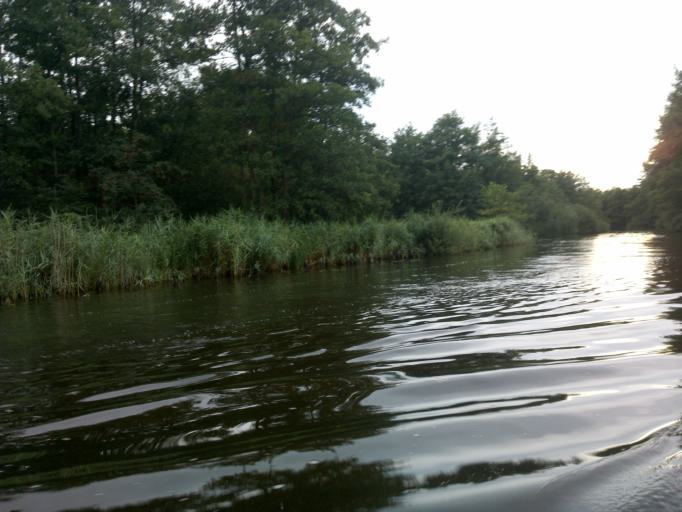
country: NL
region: North Holland
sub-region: Gemeente Wijdemeren
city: Oud-Loosdrecht
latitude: 52.2018
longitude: 5.0991
